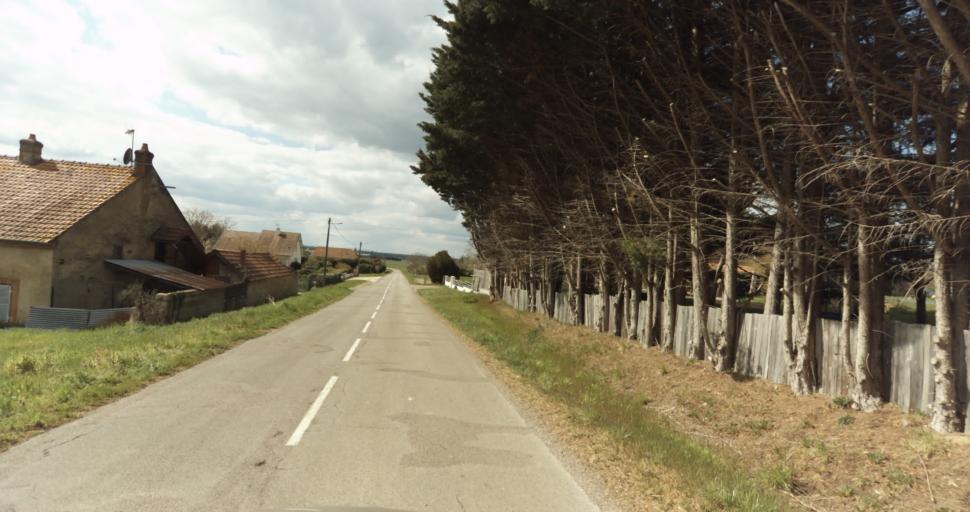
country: FR
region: Bourgogne
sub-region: Departement de la Cote-d'Or
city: Auxonne
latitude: 47.1938
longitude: 5.4306
